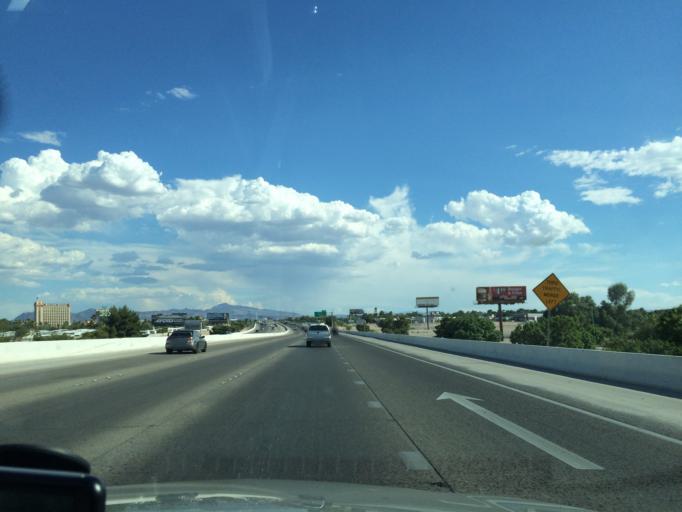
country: US
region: Nevada
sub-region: Clark County
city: Winchester
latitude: 36.1446
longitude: -115.0914
